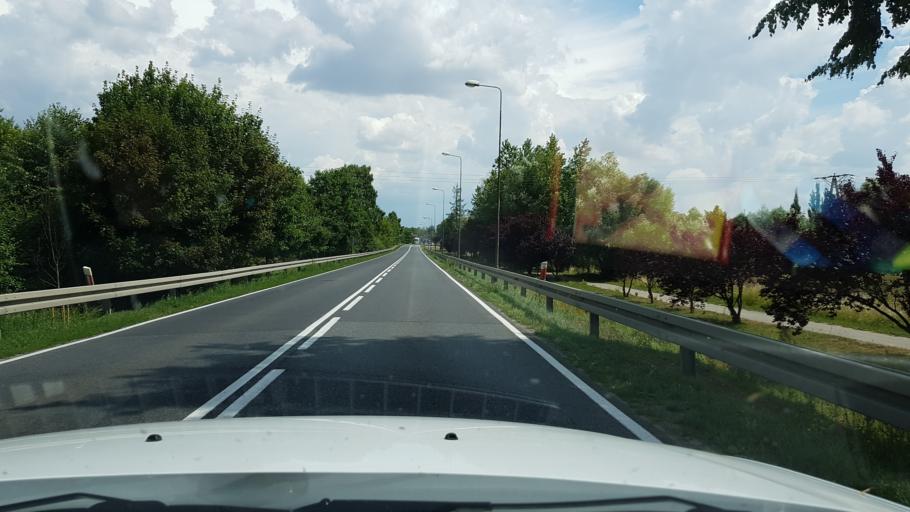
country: PL
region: West Pomeranian Voivodeship
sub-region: Powiat walecki
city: Walcz
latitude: 53.2849
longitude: 16.4461
